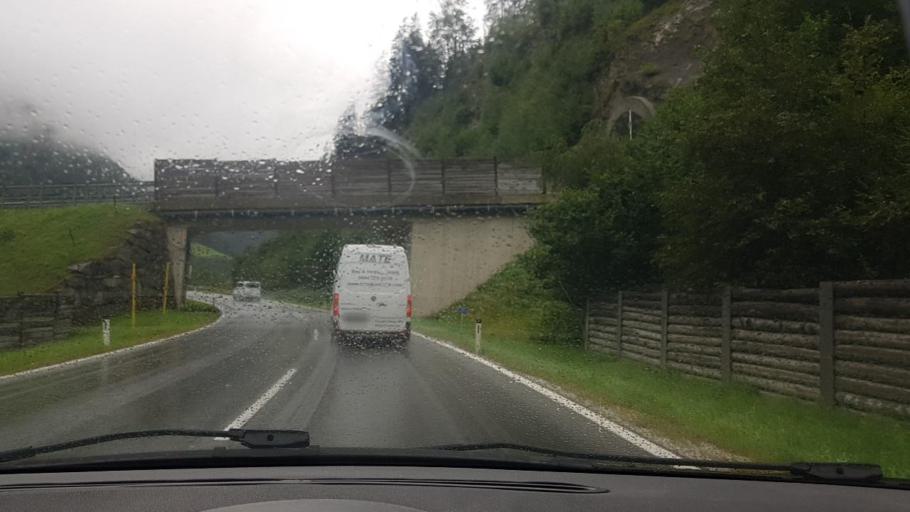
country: AT
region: Tyrol
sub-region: Politischer Bezirk Innsbruck Land
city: Steinach am Brenner
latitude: 47.0762
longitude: 11.4815
